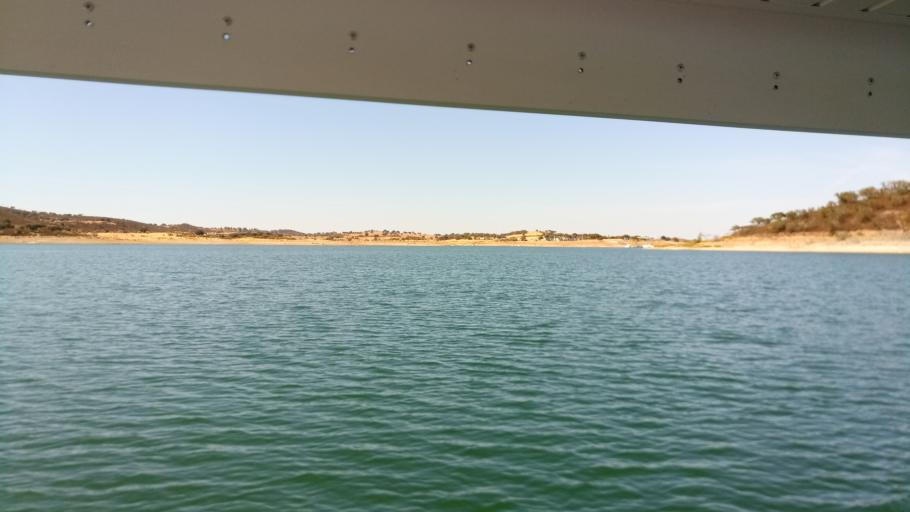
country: PT
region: Evora
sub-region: Mourao
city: Mourao
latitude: 38.4266
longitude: -7.3527
